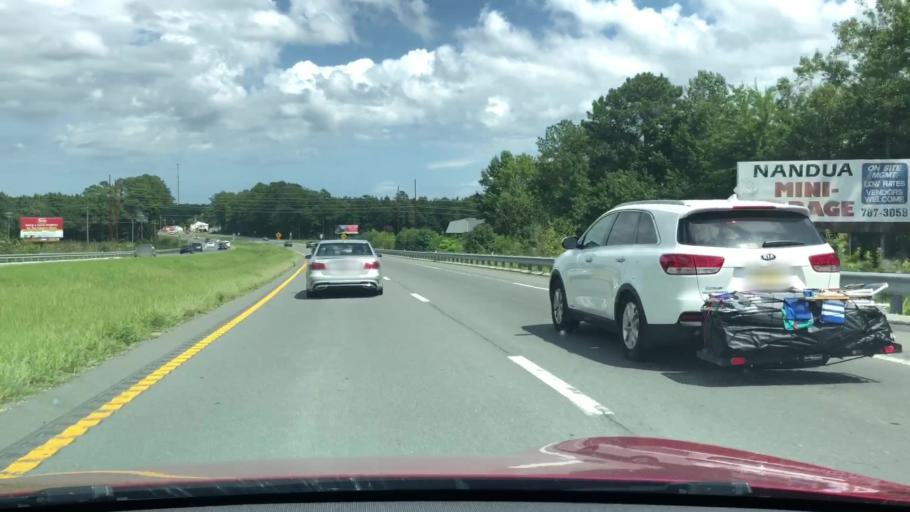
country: US
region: Virginia
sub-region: Accomack County
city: Accomac
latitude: 37.7026
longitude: -75.7051
